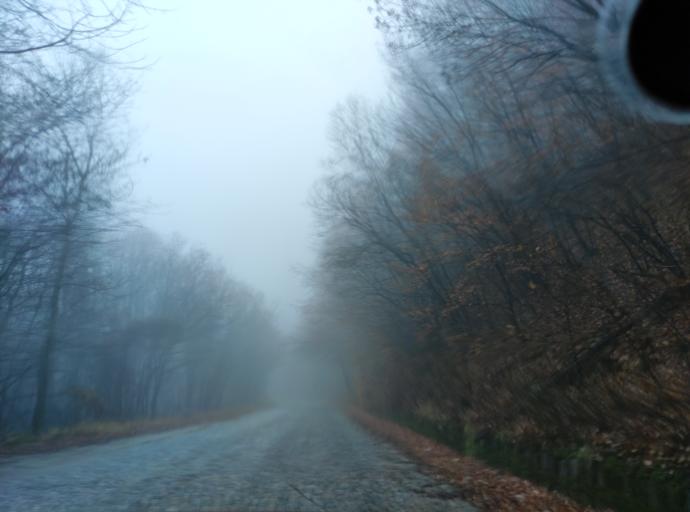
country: BG
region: Sofia-Capital
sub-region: Stolichna Obshtina
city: Sofia
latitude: 42.6246
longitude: 23.2939
